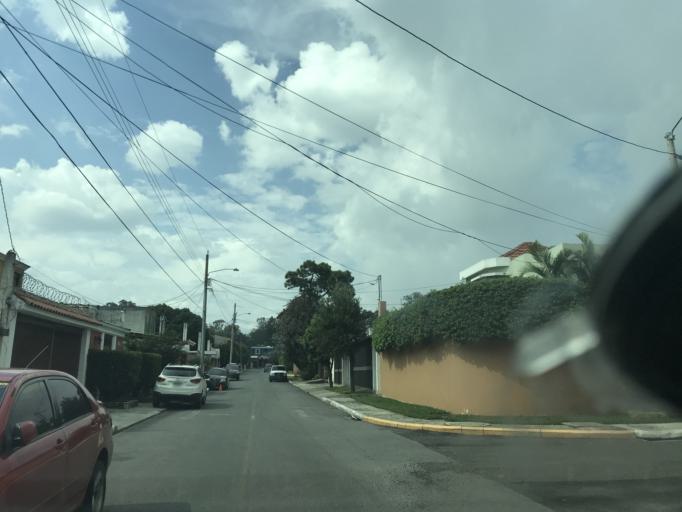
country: GT
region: Guatemala
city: Santa Catarina Pinula
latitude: 14.5811
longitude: -90.5526
